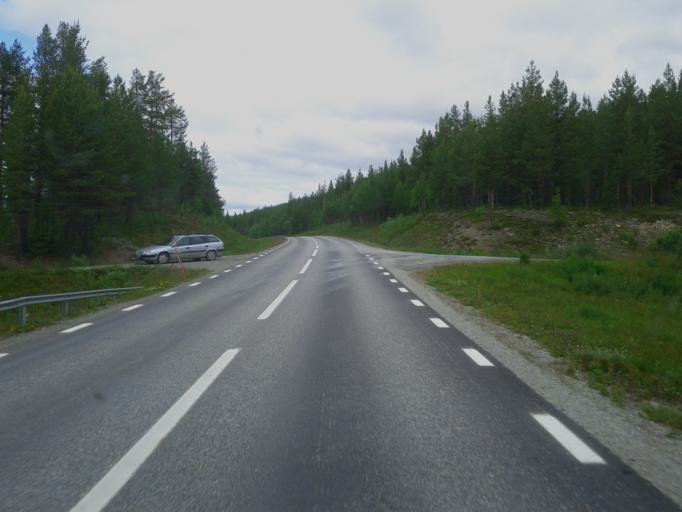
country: SE
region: Vaesterbotten
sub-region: Storumans Kommun
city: Fristad
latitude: 65.3787
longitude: 16.5139
